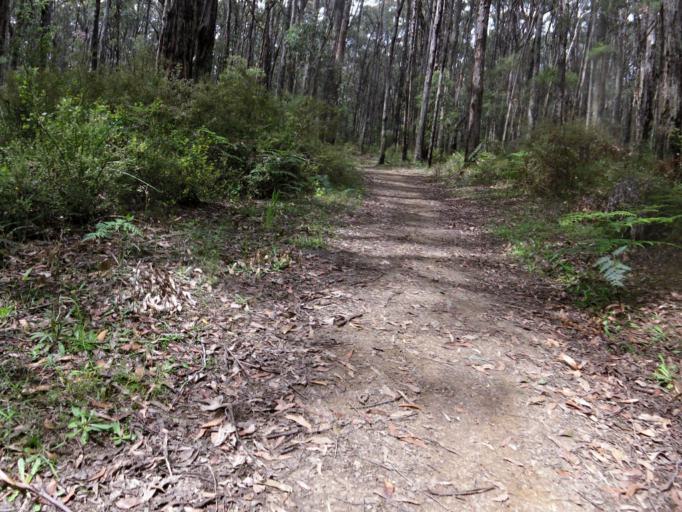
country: AU
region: Victoria
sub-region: Cardinia
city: Cockatoo
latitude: -37.9337
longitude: 145.4742
